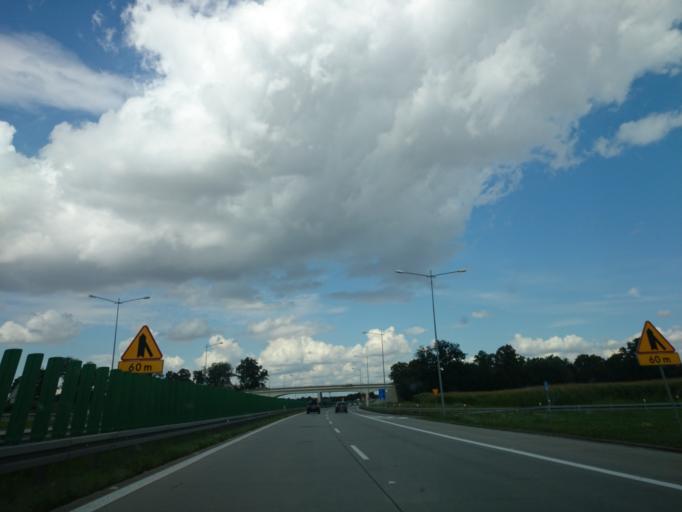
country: PL
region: Lower Silesian Voivodeship
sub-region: Powiat sredzki
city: Udanin
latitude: 51.0854
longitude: 16.4202
